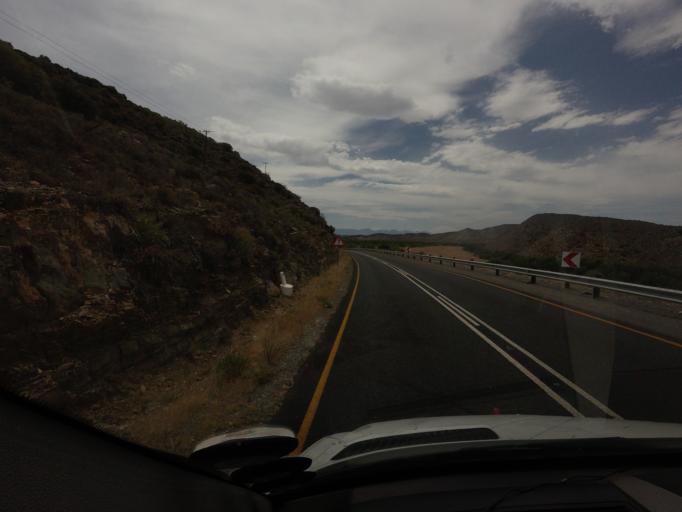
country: ZA
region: Western Cape
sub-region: Eden District Municipality
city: Riversdale
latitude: -33.7931
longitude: 20.9259
